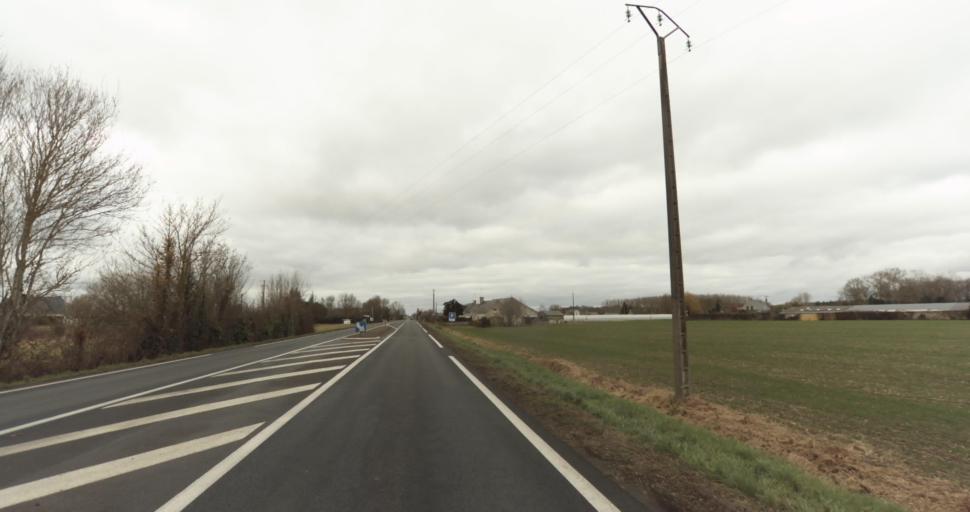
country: FR
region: Pays de la Loire
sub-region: Departement de Maine-et-Loire
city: Vivy
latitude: 47.3144
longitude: -0.0450
